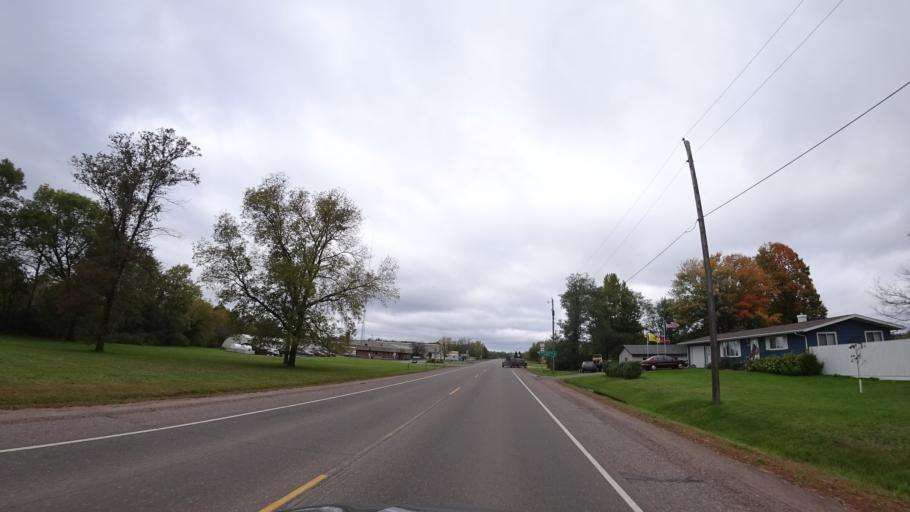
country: US
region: Wisconsin
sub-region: Rusk County
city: Ladysmith
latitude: 45.4750
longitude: -91.1109
